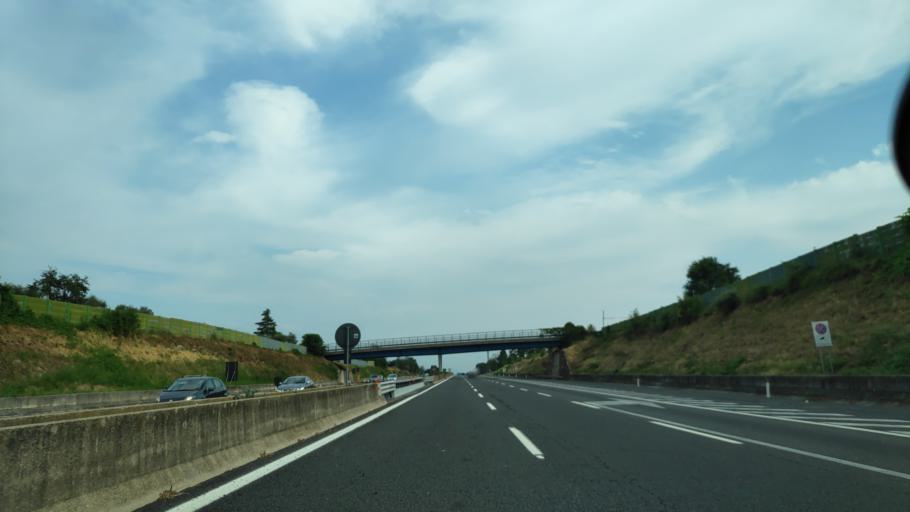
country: IT
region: Latium
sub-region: Citta metropolitana di Roma Capitale
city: Fiano Romano
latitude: 42.1747
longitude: 12.6069
